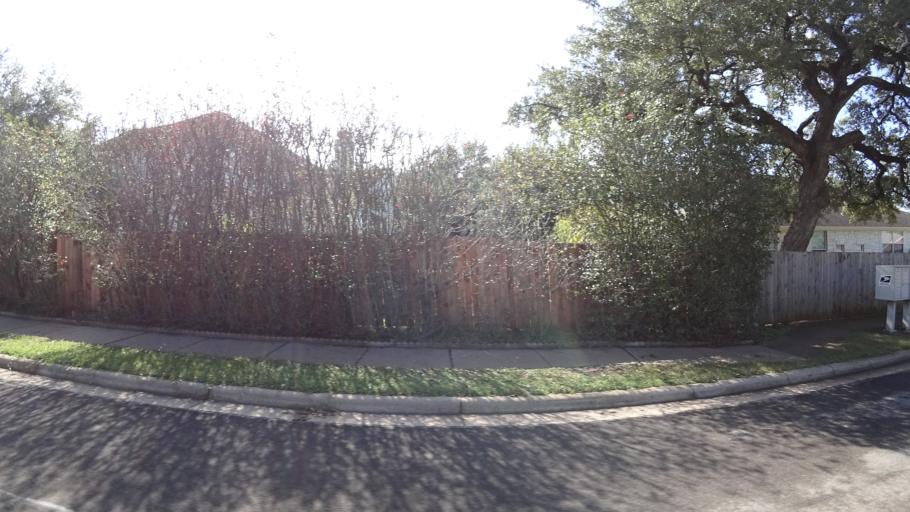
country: US
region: Texas
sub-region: Travis County
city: Shady Hollow
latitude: 30.2090
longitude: -97.8757
